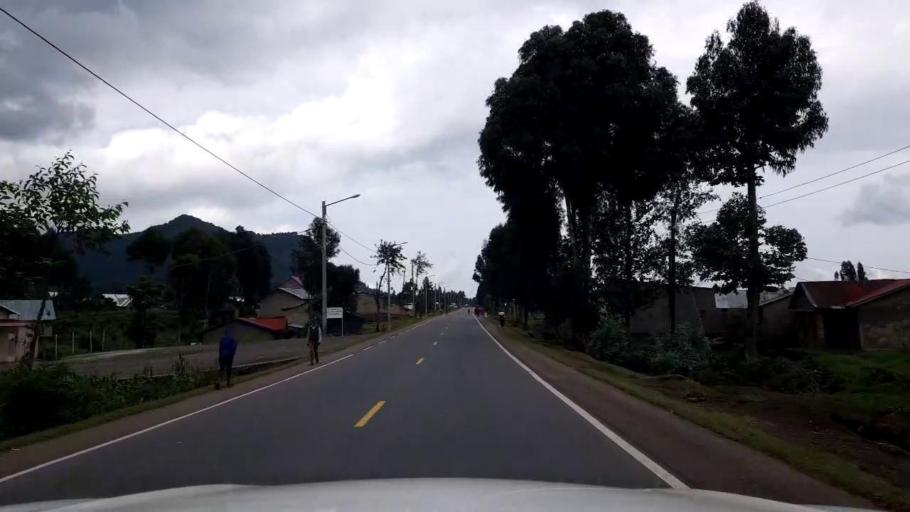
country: RW
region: Western Province
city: Gisenyi
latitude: -1.6346
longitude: 29.4100
